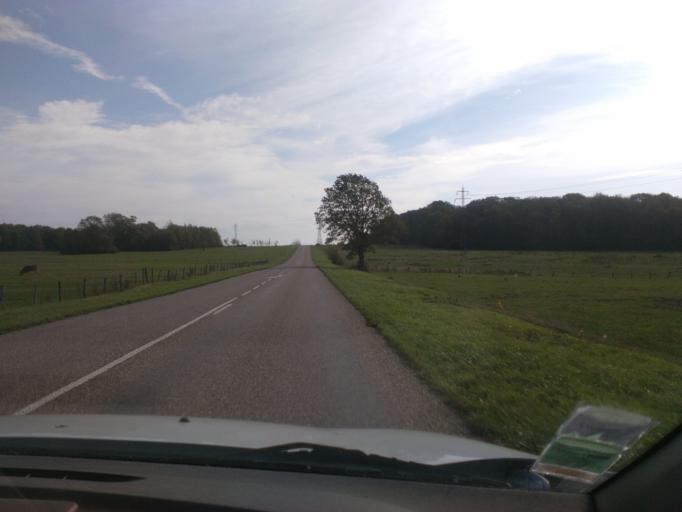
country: FR
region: Lorraine
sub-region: Departement des Vosges
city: Chatel-sur-Moselle
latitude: 48.3444
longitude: 6.4448
